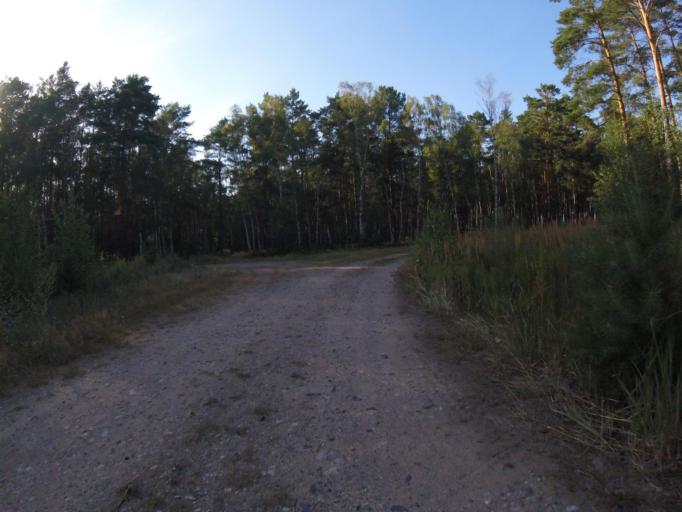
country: DE
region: Berlin
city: Schmockwitz
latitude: 52.3374
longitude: 13.7083
